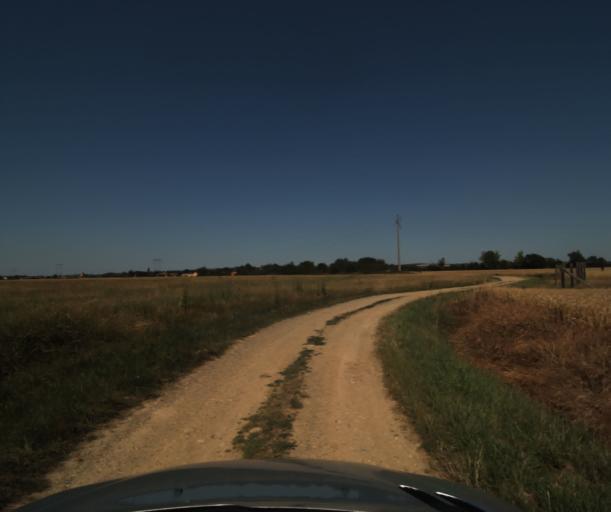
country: FR
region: Midi-Pyrenees
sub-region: Departement de la Haute-Garonne
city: Muret
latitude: 43.4650
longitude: 1.3714
